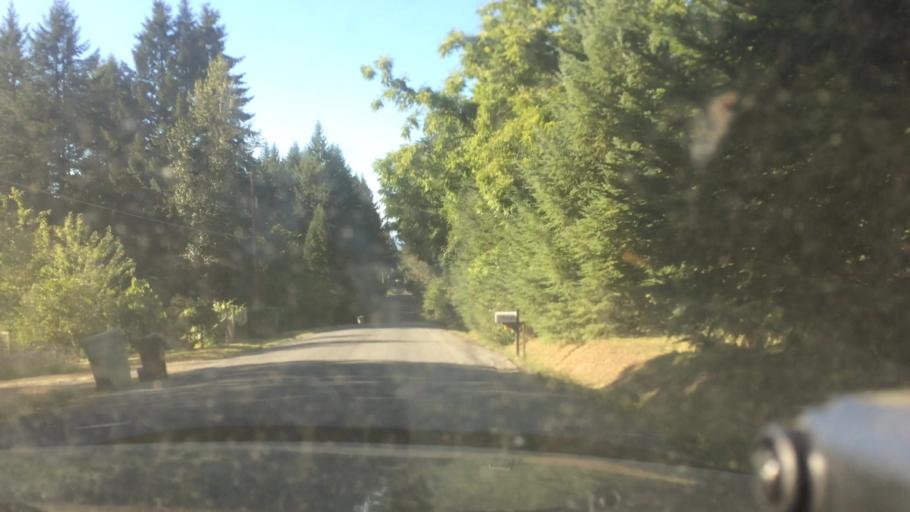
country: US
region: Oregon
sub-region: Yamhill County
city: Newberg
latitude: 45.3756
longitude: -122.9755
